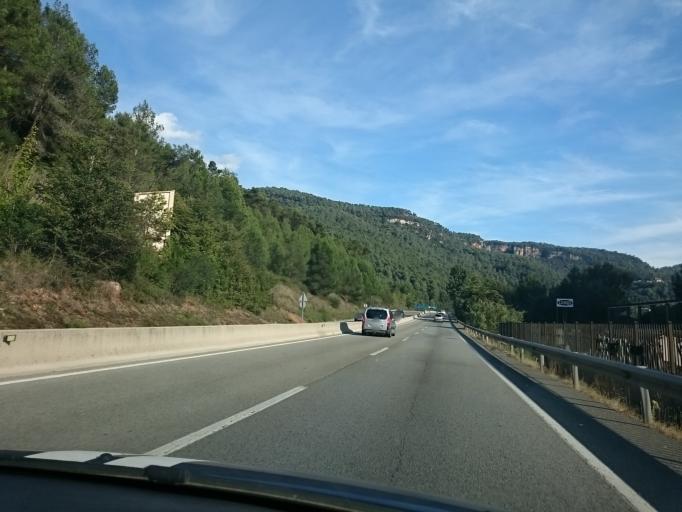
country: ES
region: Catalonia
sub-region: Provincia de Barcelona
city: Tagamanent
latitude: 41.7503
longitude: 2.2584
